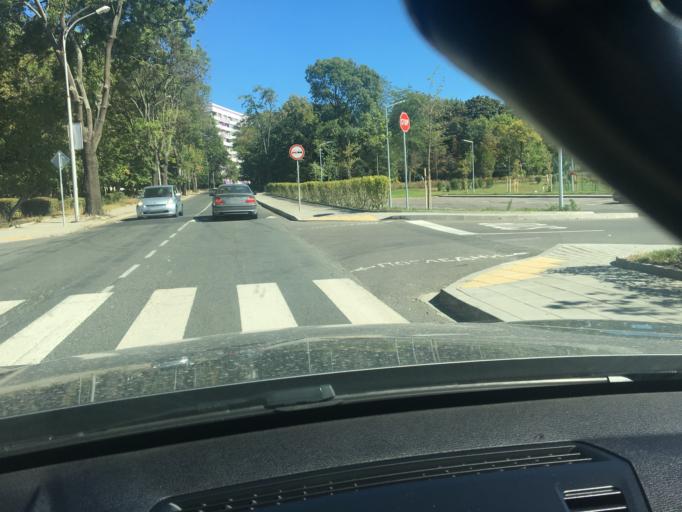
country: BG
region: Burgas
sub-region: Obshtina Burgas
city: Burgas
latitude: 42.5133
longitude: 27.4583
